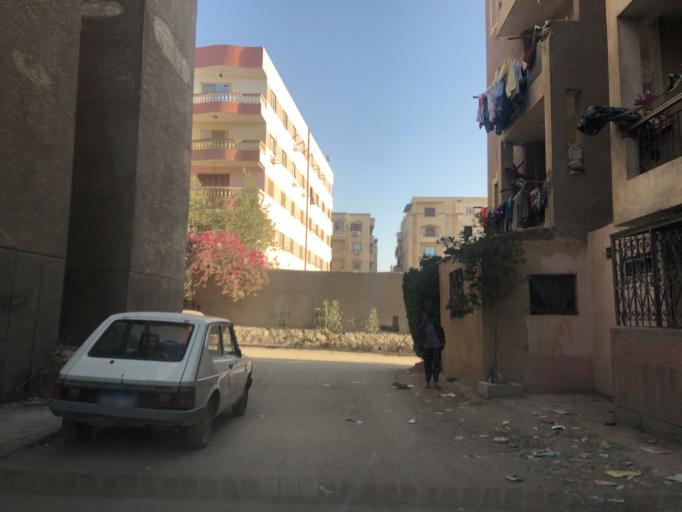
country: EG
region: Al Jizah
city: Al Jizah
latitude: 29.9884
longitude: 31.1023
